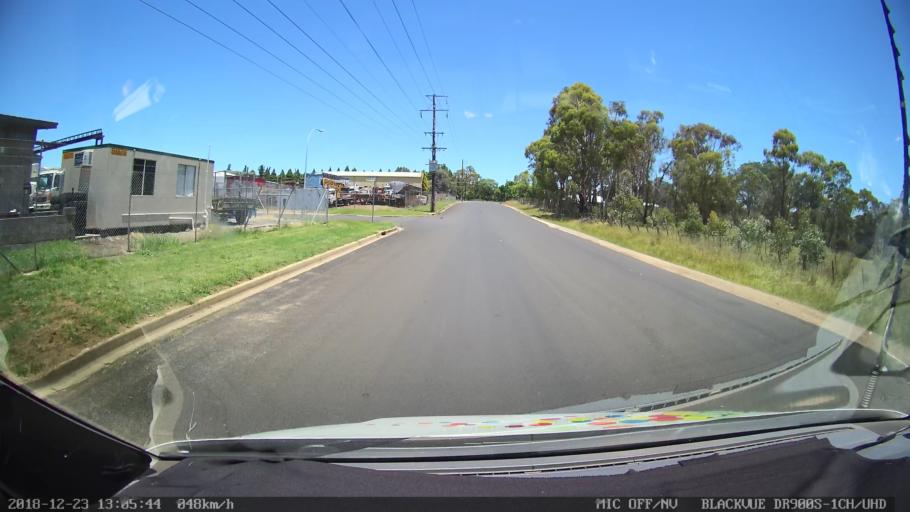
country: AU
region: New South Wales
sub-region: Armidale Dumaresq
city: Armidale
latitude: -30.5154
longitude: 151.6410
